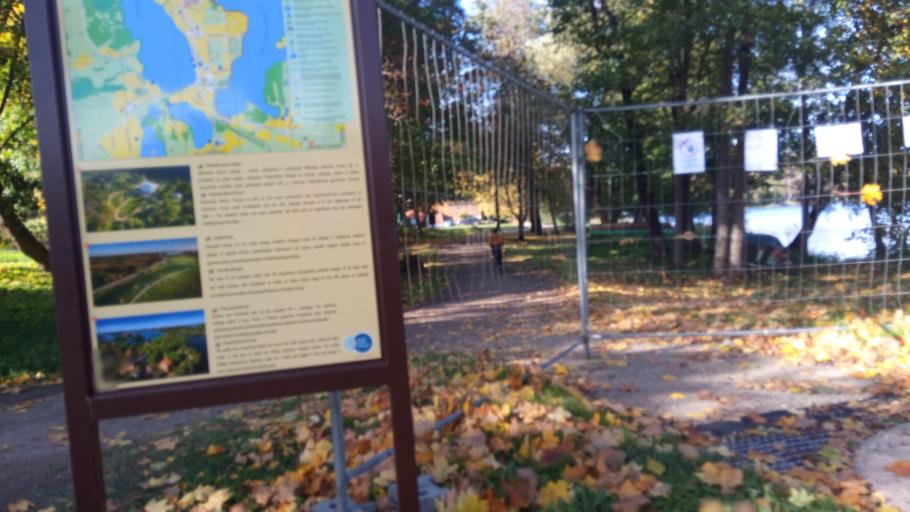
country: LT
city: Trakai
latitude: 54.6409
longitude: 24.9380
